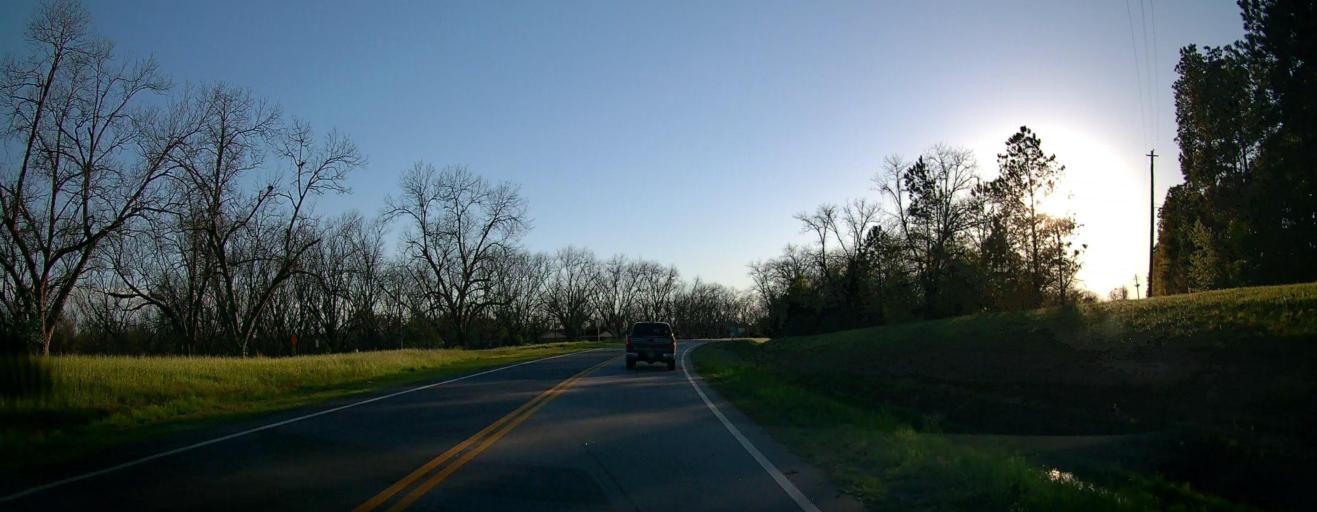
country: US
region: Georgia
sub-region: Wilcox County
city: Rochelle
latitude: 31.9521
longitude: -83.4391
